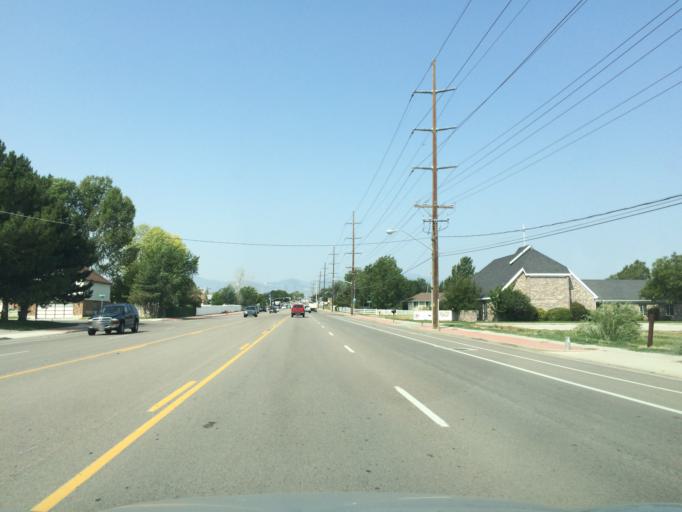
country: US
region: Utah
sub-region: Salt Lake County
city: South Jordan Heights
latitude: 40.5878
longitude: -111.9622
